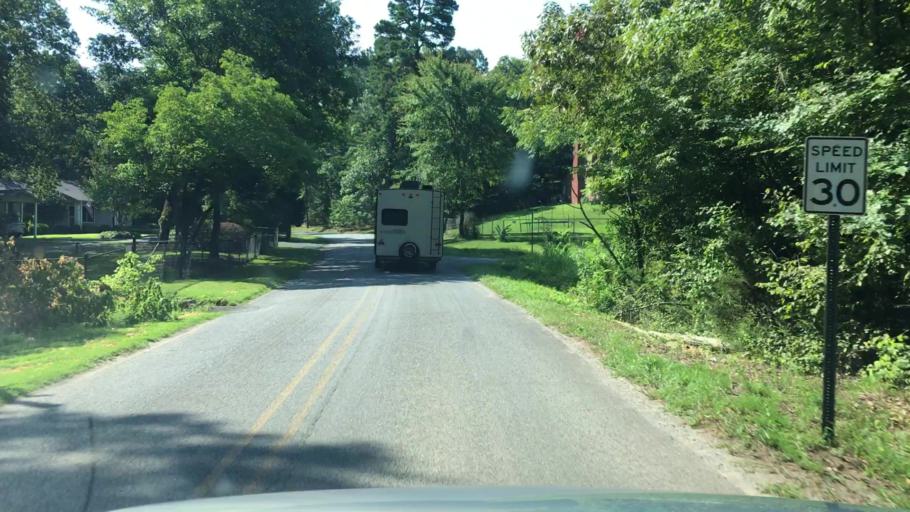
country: US
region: Arkansas
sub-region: Garland County
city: Piney
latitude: 34.5318
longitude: -93.3380
